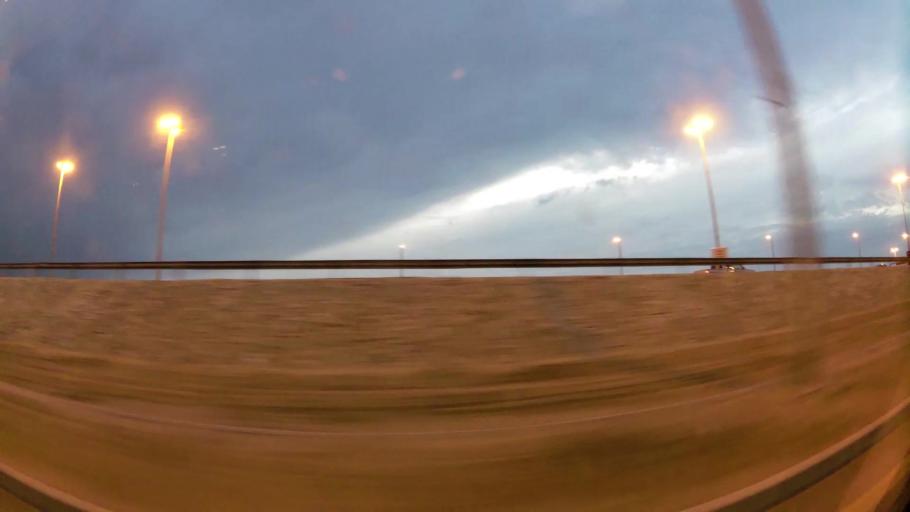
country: BH
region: Central Governorate
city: Madinat Hamad
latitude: 26.1432
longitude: 50.5106
